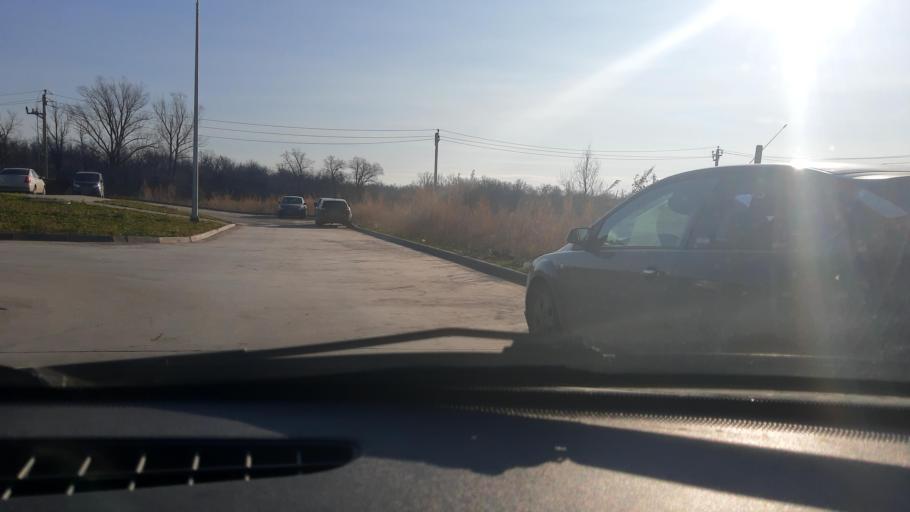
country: RU
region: Bashkortostan
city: Mikhaylovka
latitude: 54.6985
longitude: 55.8628
